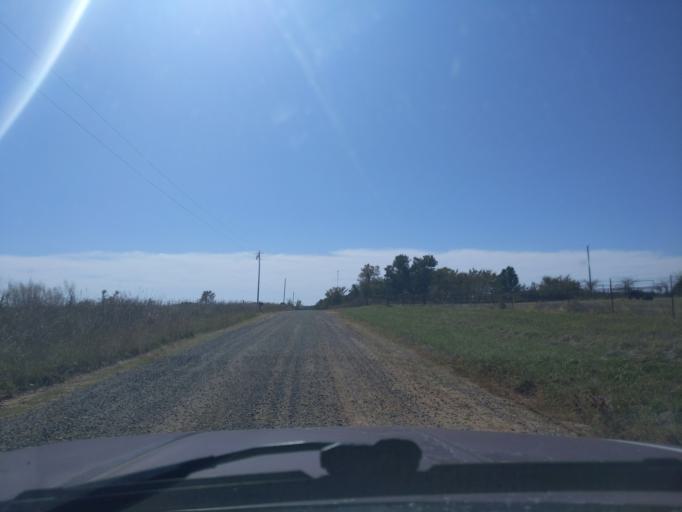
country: US
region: Oklahoma
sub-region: Okfuskee County
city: Boley
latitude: 35.6474
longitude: -96.4235
